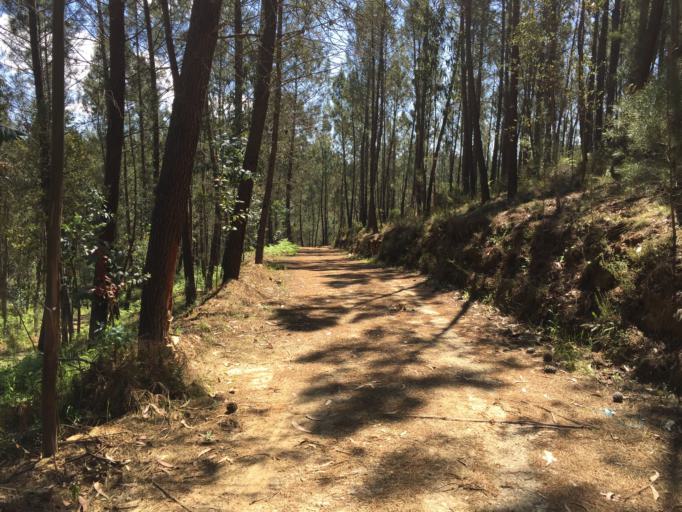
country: PT
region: Coimbra
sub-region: Pampilhosa da Serra
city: Pampilhosa da Serra
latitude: 40.0757
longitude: -7.7789
